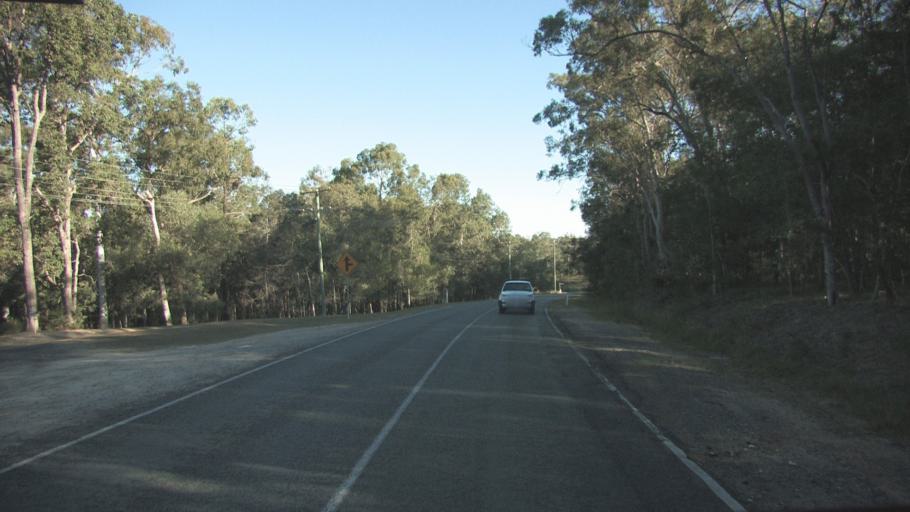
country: AU
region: Queensland
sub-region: Logan
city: Chambers Flat
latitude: -27.7558
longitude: 153.0495
